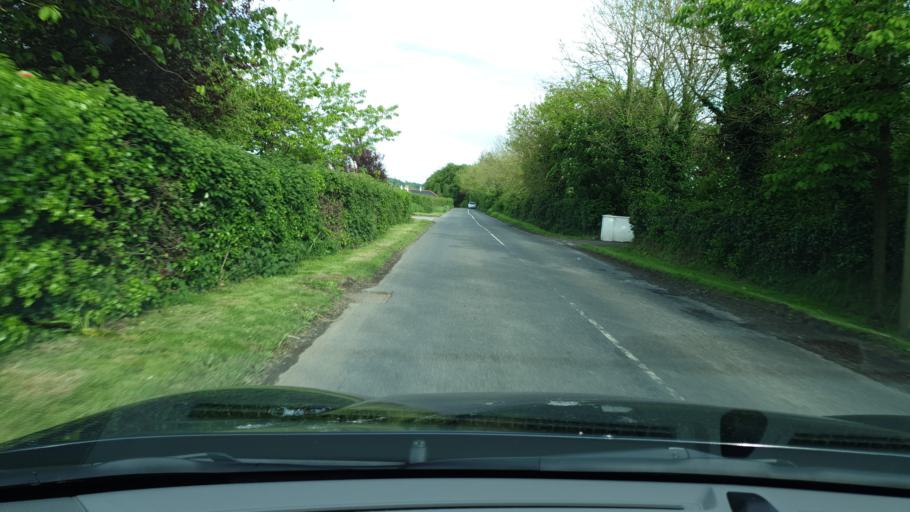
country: IE
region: Leinster
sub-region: An Mhi
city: Ashbourne
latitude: 53.5623
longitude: -6.3446
